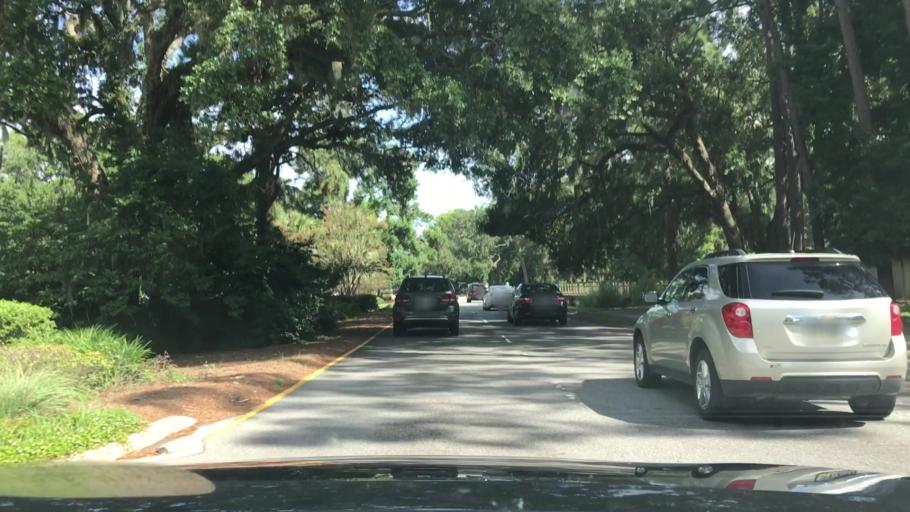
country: US
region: South Carolina
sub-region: Beaufort County
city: Hilton Head Island
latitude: 32.1516
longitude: -80.7595
